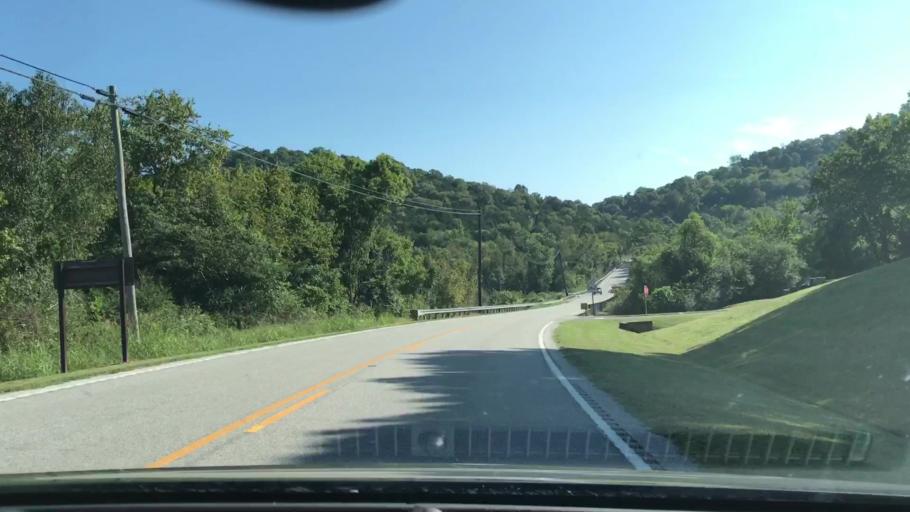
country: US
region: Tennessee
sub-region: Jackson County
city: Gainesboro
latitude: 36.3611
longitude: -85.7763
